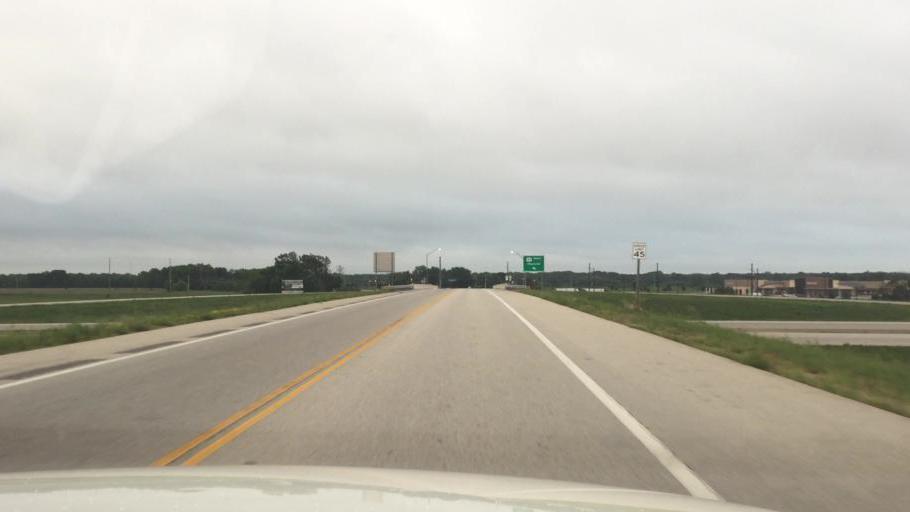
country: US
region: Kansas
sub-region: Montgomery County
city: Coffeyville
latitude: 37.0471
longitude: -95.5839
